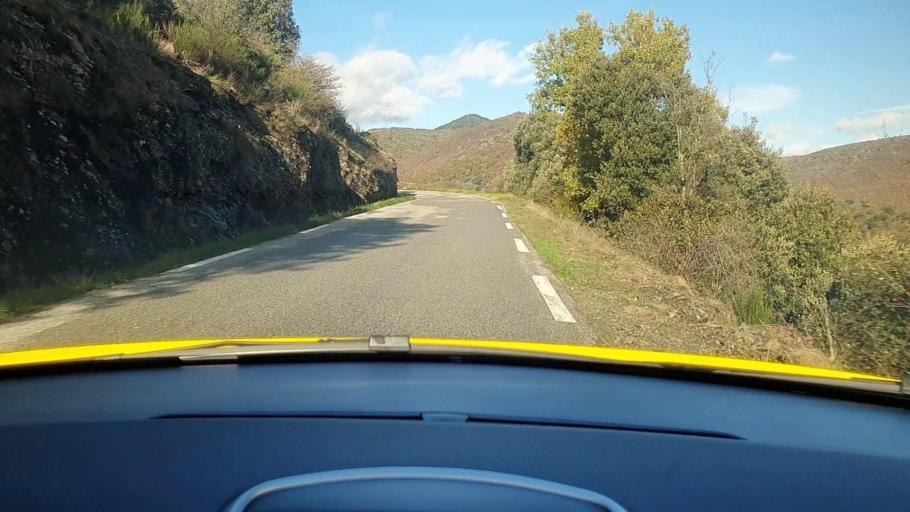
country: FR
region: Languedoc-Roussillon
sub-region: Departement du Gard
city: Valleraugue
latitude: 44.1648
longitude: 3.6371
